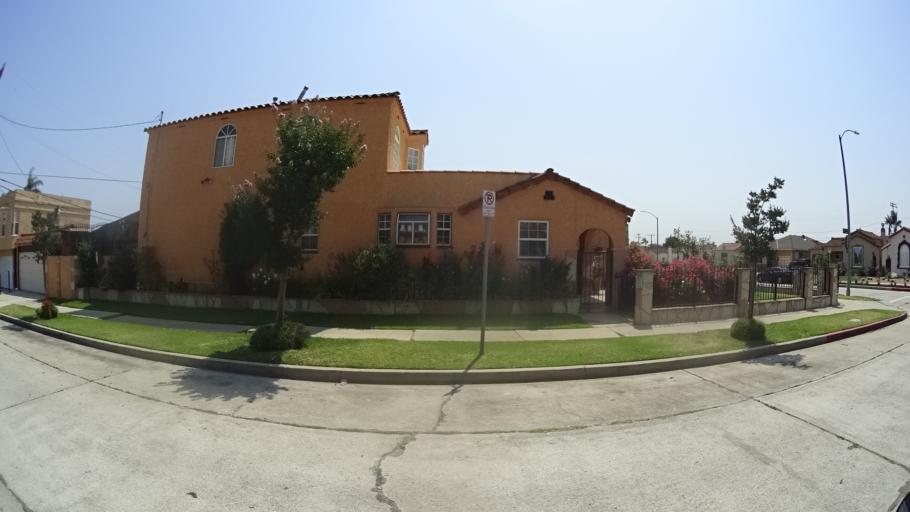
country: US
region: California
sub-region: Los Angeles County
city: Inglewood
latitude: 33.9702
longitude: -118.3286
